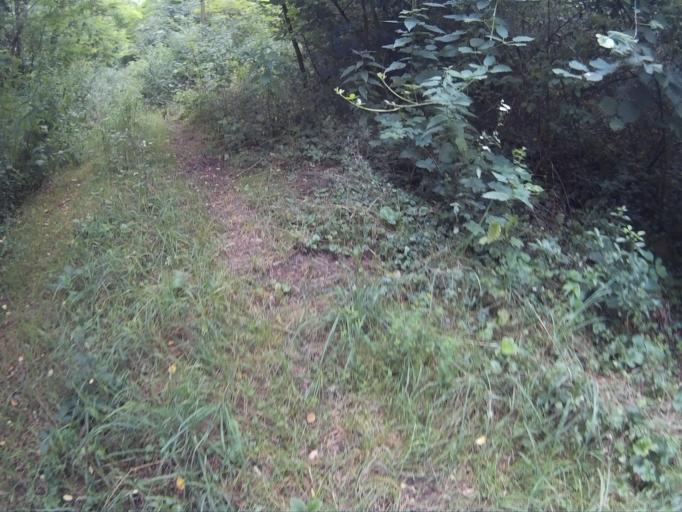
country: HU
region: Veszprem
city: Papa
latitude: 47.2794
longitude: 17.5619
